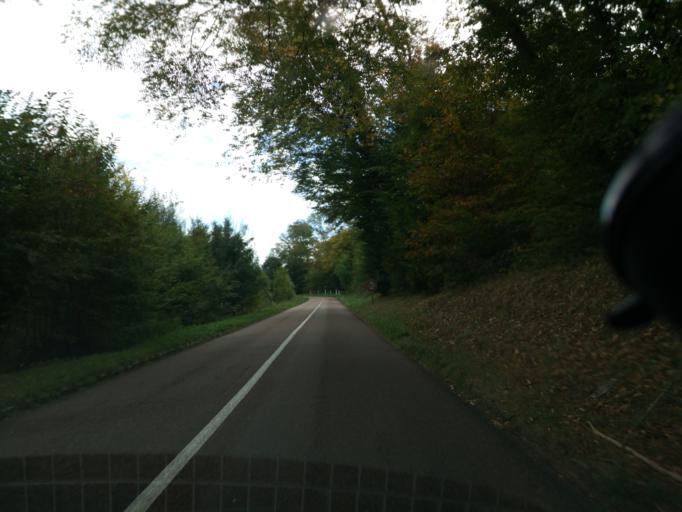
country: FR
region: Ile-de-France
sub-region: Departement de l'Essonne
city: Les Molieres
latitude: 48.6834
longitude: 2.0708
